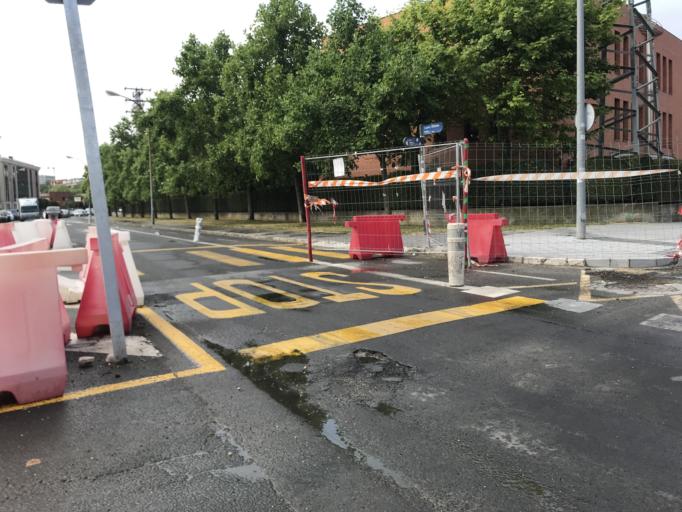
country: ES
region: Basque Country
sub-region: Provincia de Alava
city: Gasteiz / Vitoria
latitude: 42.8401
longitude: -2.6634
